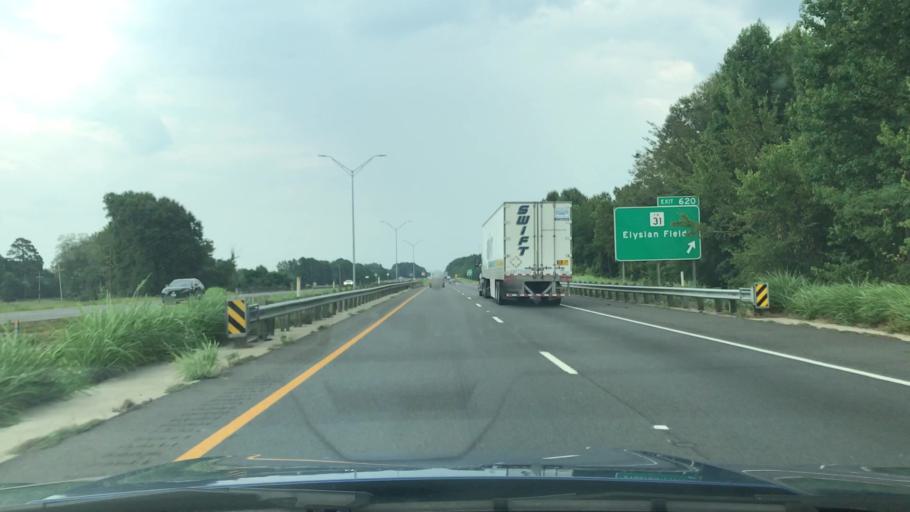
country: US
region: Texas
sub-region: Harrison County
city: Marshall
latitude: 32.4933
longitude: -94.3023
